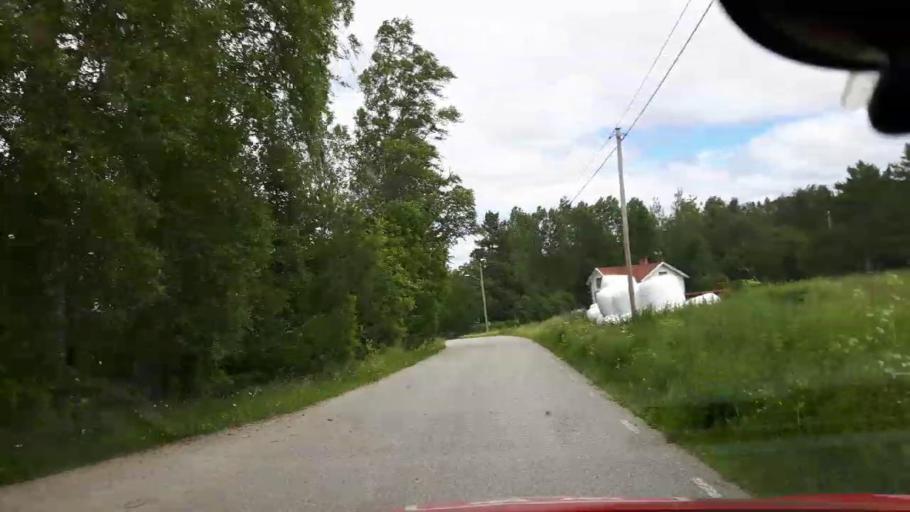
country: SE
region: Jaemtland
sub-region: Braecke Kommun
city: Braecke
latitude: 62.8772
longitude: 15.2749
